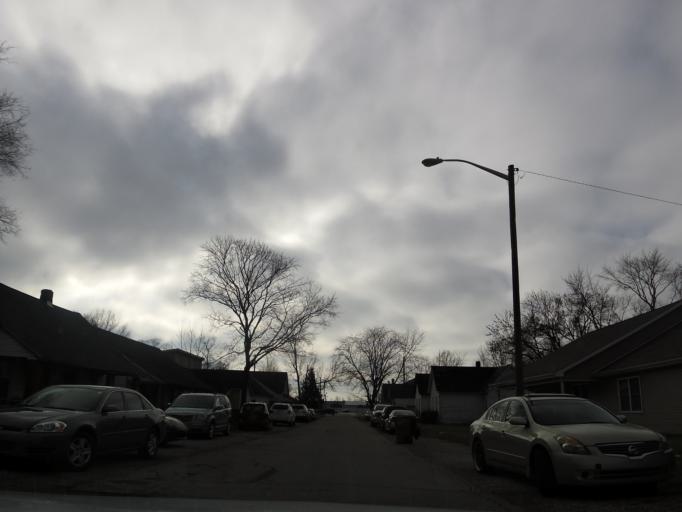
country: US
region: Indiana
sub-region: Bartholomew County
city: Columbus
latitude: 39.1989
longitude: -85.8957
